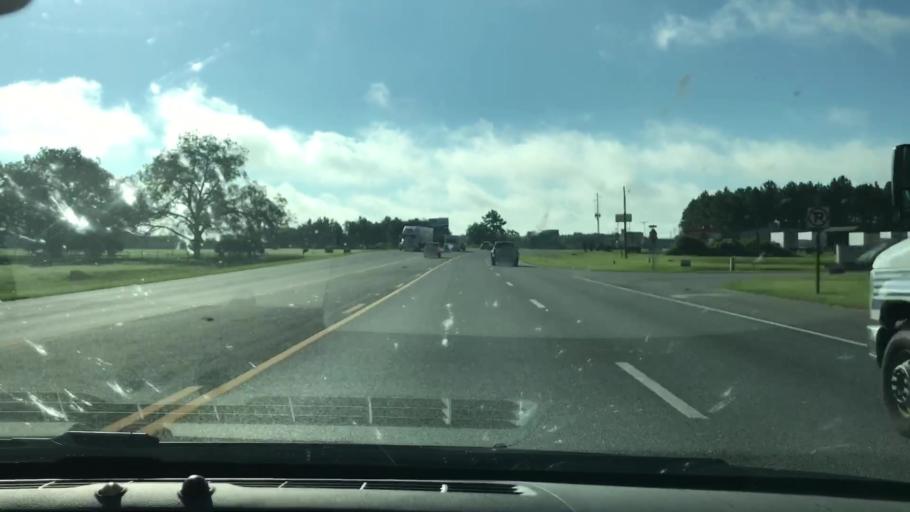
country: US
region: Georgia
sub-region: Terrell County
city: Dawson
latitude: 31.7575
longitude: -84.4288
